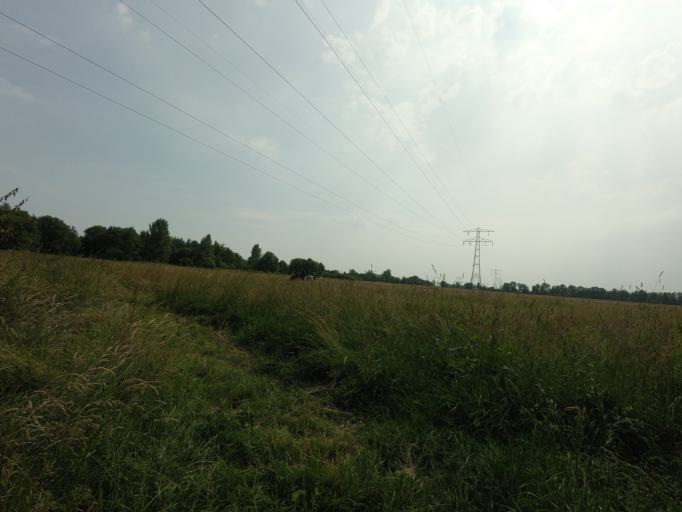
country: NL
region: South Holland
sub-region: Gemeente Gouda
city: Gouda
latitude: 51.9776
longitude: 4.6976
